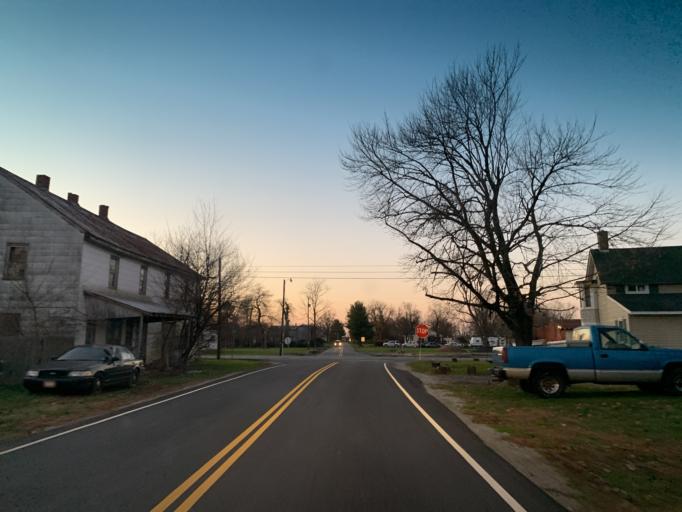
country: US
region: Delaware
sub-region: New Castle County
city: Middletown
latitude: 39.4189
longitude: -75.7744
